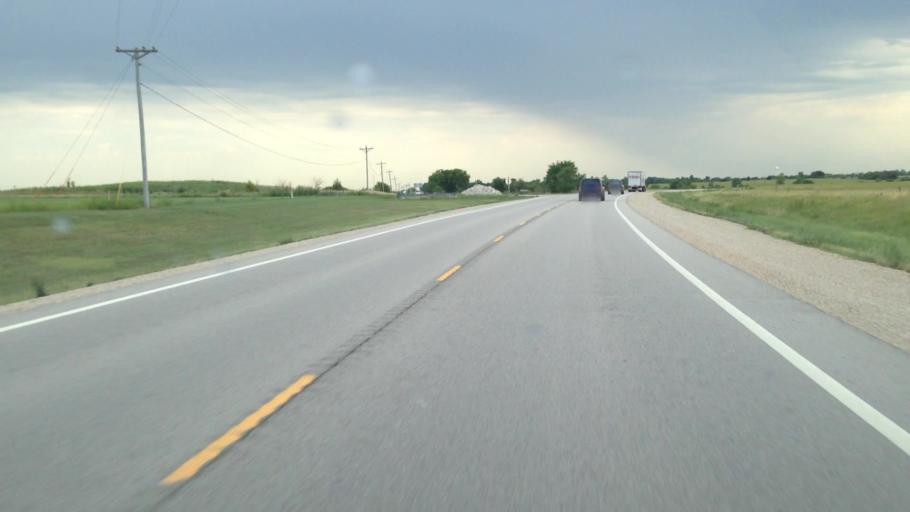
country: US
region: Kansas
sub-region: Coffey County
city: Burlington
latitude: 38.3009
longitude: -95.7290
